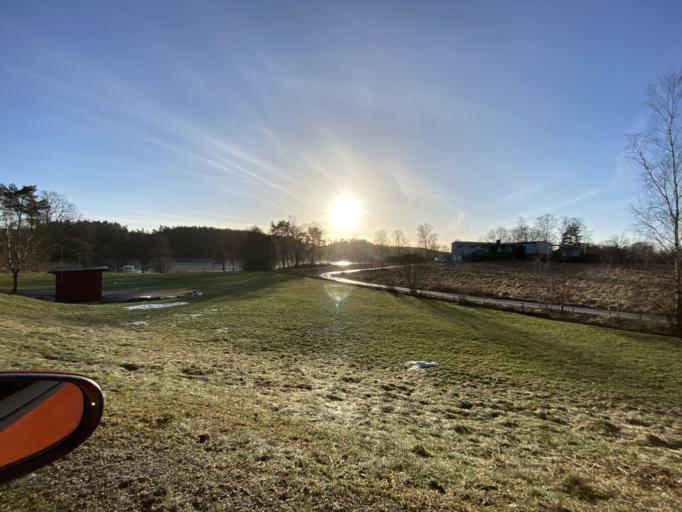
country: SE
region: Stockholm
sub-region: Salems Kommun
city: Ronninge
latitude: 59.1834
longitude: 17.7308
